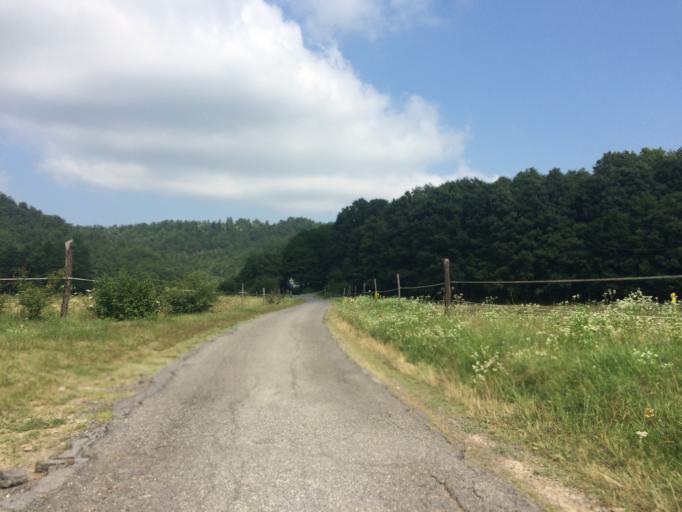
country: IT
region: Liguria
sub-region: Provincia di Savona
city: Dego
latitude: 44.4643
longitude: 8.3497
